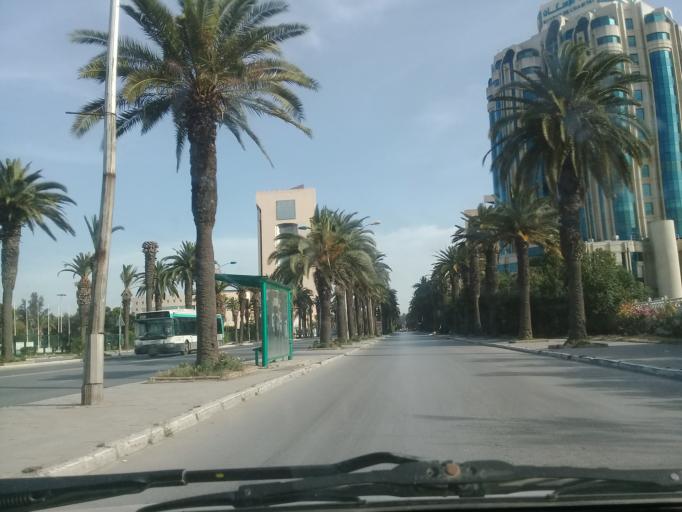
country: TN
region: Tunis
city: Tunis
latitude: 36.8065
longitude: 10.1852
